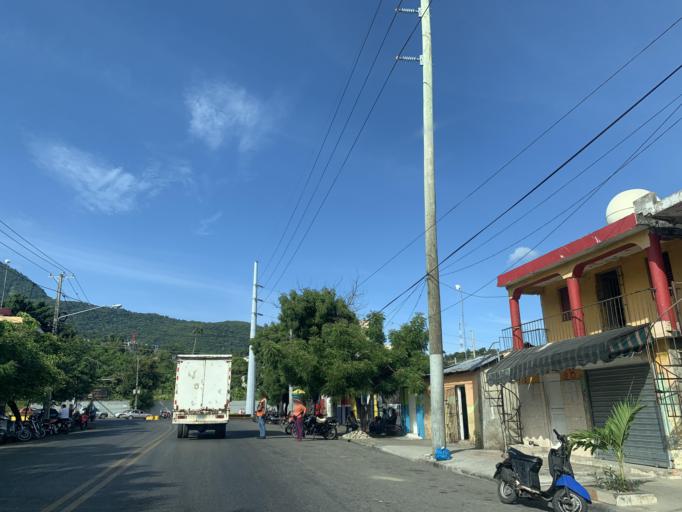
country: DO
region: Puerto Plata
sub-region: Puerto Plata
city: Puerto Plata
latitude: 19.7926
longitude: -70.7043
